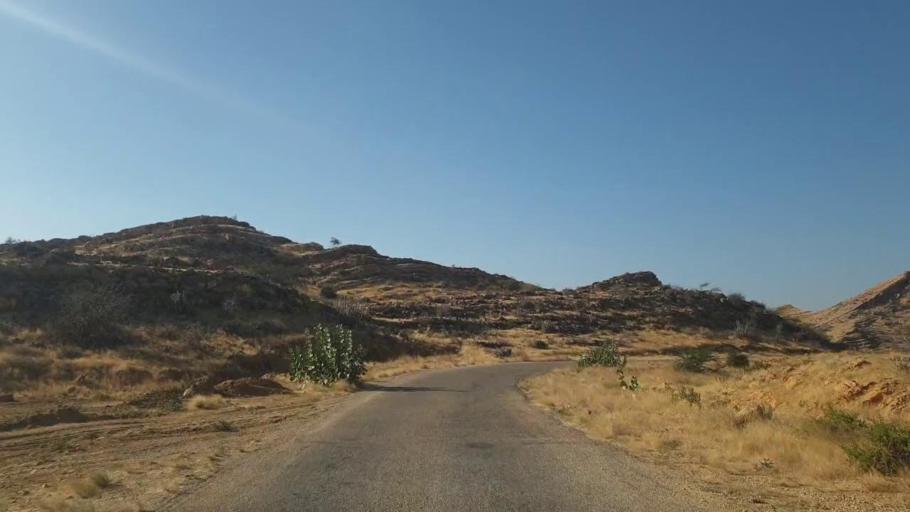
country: PK
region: Sindh
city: Malir Cantonment
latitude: 25.4029
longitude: 67.4853
